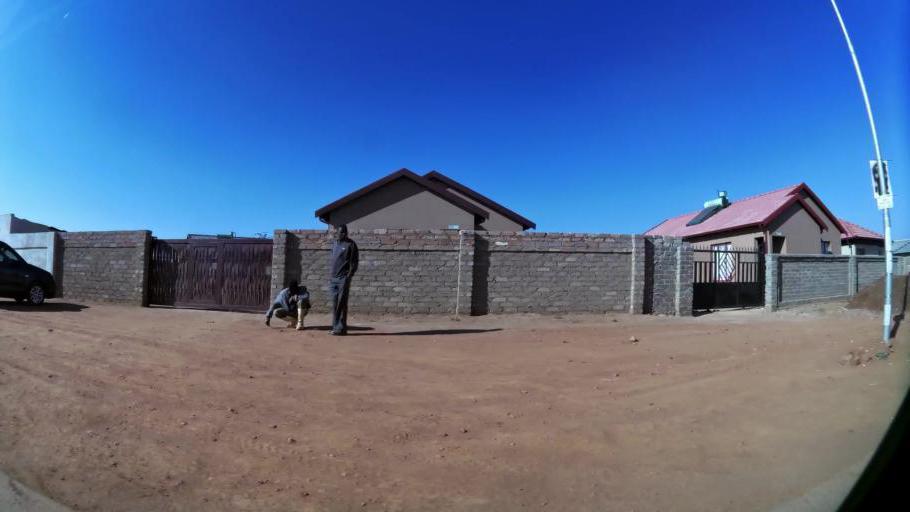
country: ZA
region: Gauteng
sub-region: City of Tshwane Metropolitan Municipality
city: Mabopane
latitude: -25.5581
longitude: 28.0962
